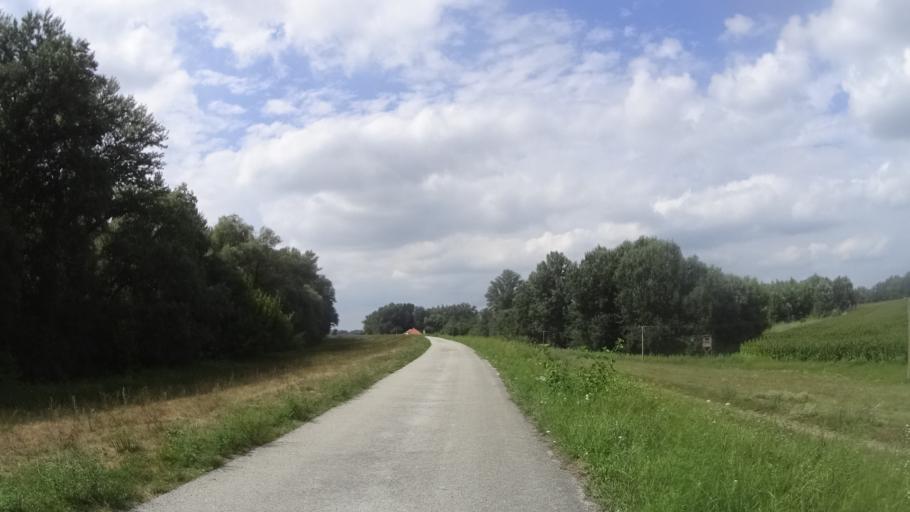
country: SK
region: Trnavsky
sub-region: Okres Dunajska Streda
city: Velky Meder
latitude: 47.7897
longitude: 17.6917
